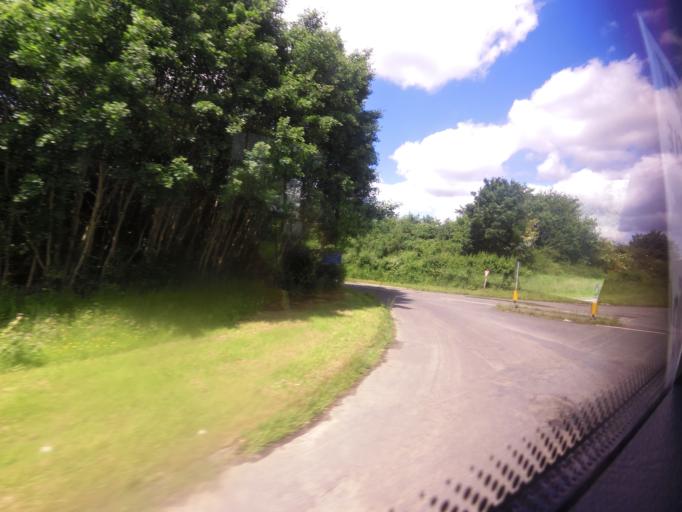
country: GB
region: England
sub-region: Norfolk
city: Aylsham
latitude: 52.8196
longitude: 1.2742
